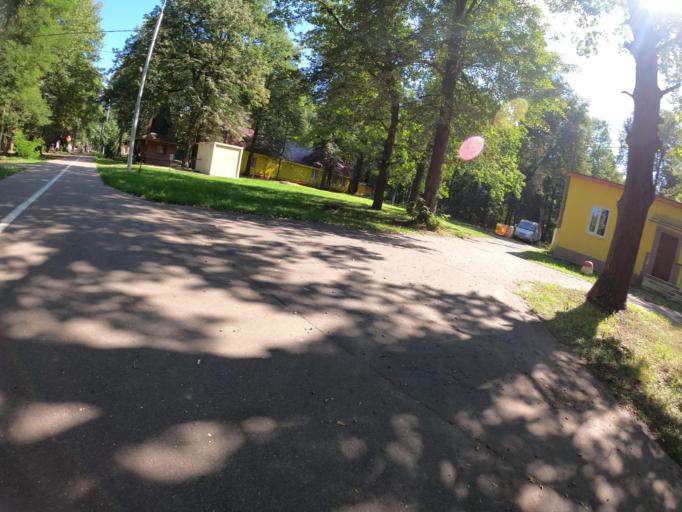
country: RU
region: Moskovskaya
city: Stupino
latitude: 54.8810
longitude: 38.0843
